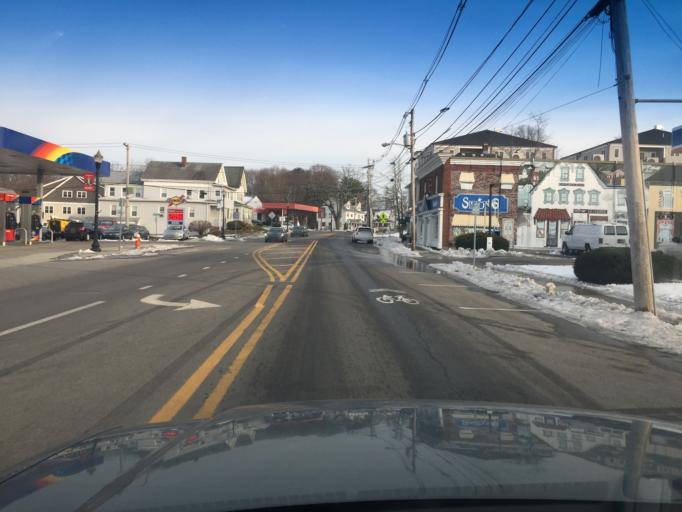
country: US
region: Massachusetts
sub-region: Norfolk County
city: Franklin
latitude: 42.0822
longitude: -71.3954
